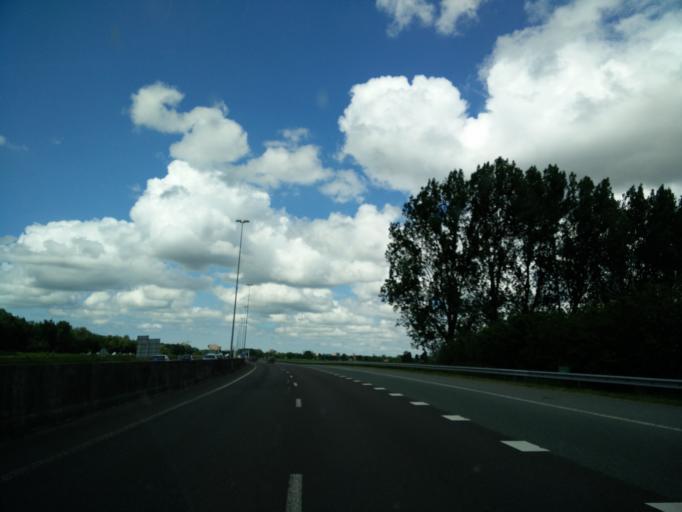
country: NL
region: Groningen
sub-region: Gemeente Haren
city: Haren
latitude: 53.1719
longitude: 6.5895
